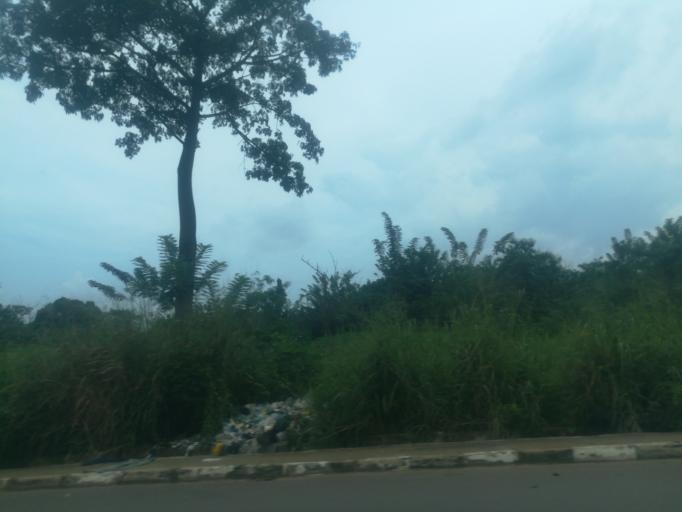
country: NG
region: Oyo
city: Ibadan
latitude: 7.3769
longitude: 3.8287
